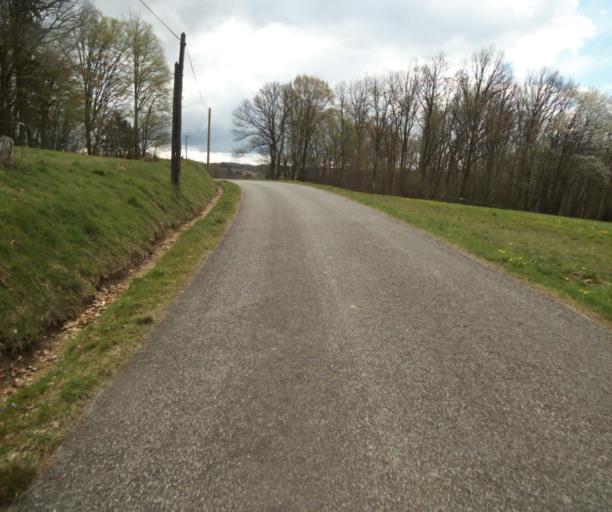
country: FR
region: Limousin
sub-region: Departement de la Correze
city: Laguenne
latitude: 45.2357
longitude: 1.8917
